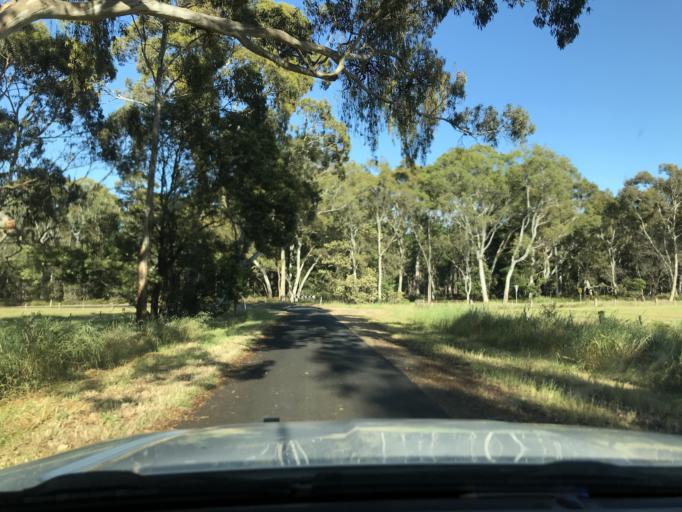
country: AU
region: South Australia
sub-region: Wattle Range
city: Penola
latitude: -37.1997
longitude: 140.9724
